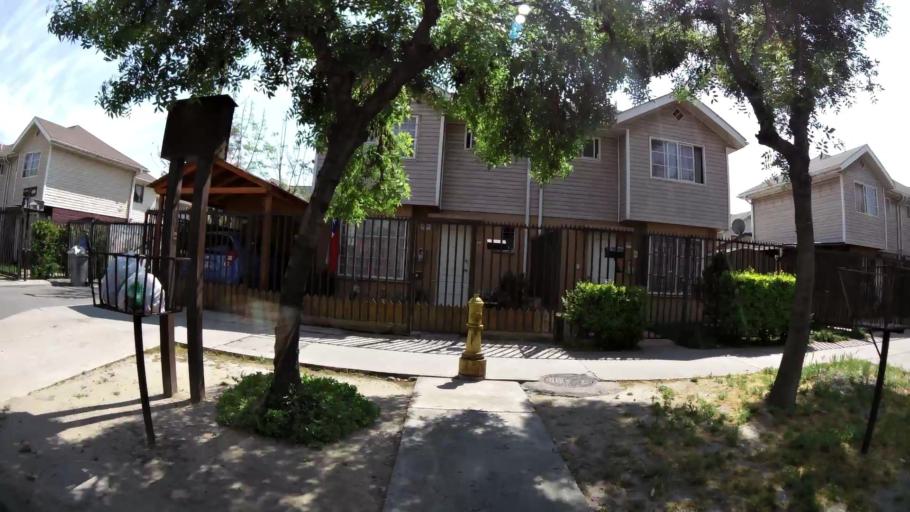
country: CL
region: Santiago Metropolitan
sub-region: Provincia de Cordillera
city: Puente Alto
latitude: -33.5922
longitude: -70.5866
